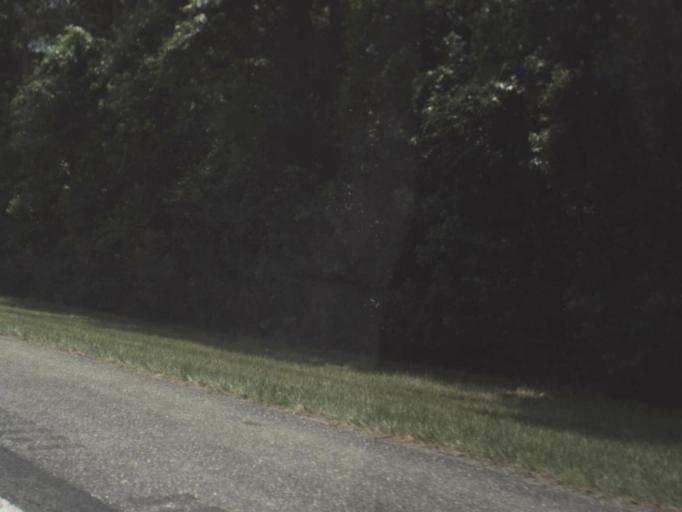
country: US
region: Florida
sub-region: Jefferson County
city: Monticello
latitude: 30.4446
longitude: -83.6882
